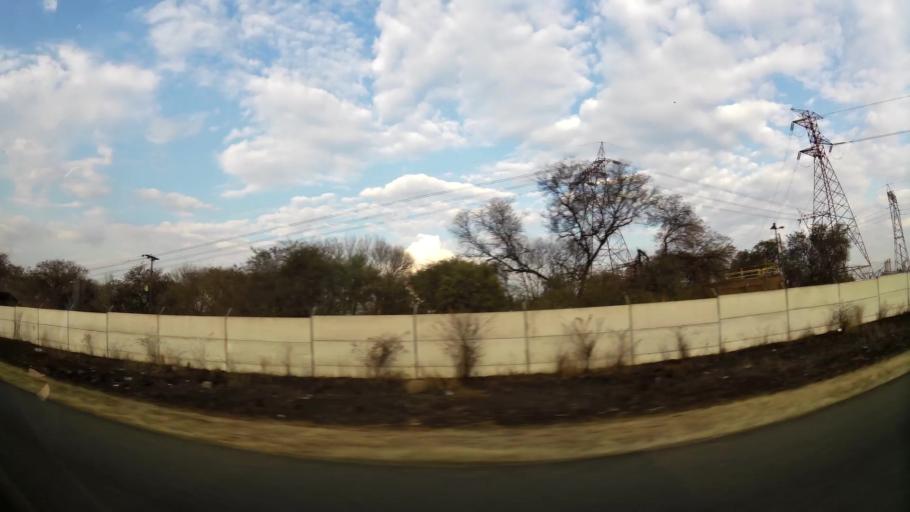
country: ZA
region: Gauteng
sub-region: Sedibeng District Municipality
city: Vanderbijlpark
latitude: -26.6633
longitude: 27.7978
